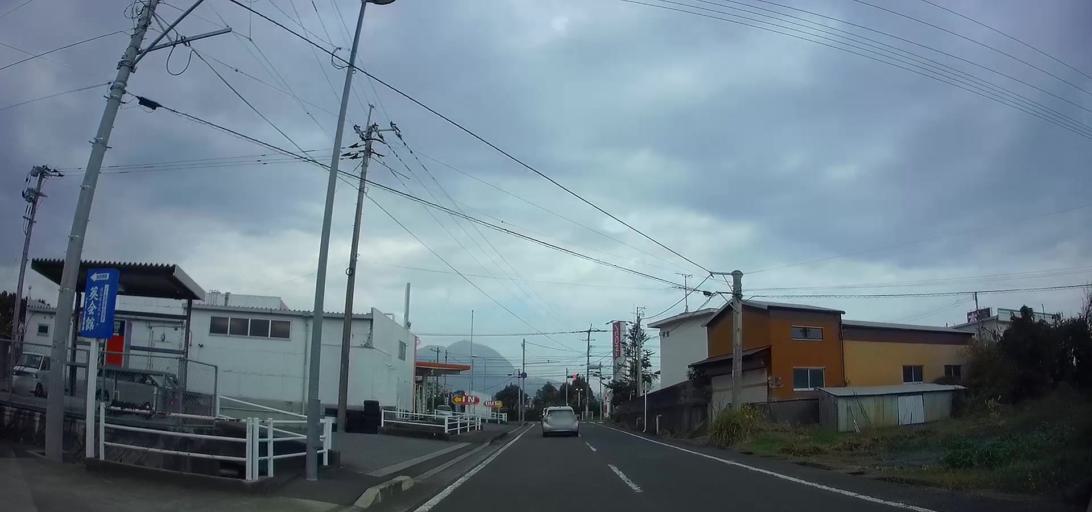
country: JP
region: Nagasaki
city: Shimabara
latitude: 32.6620
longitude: 130.3105
